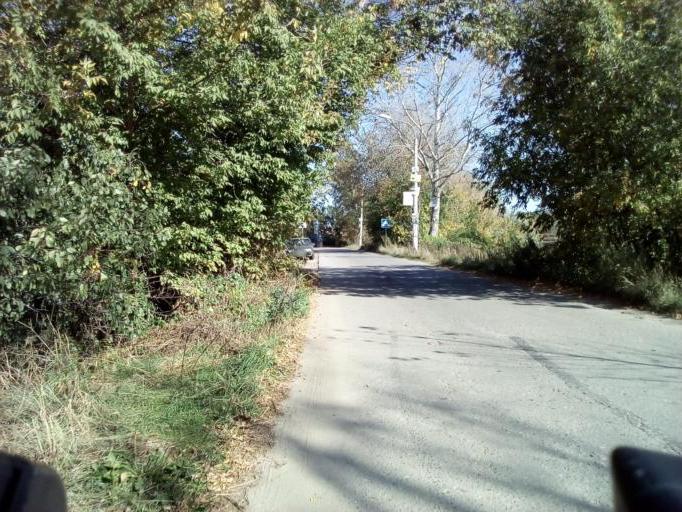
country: RU
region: Moskovskaya
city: Ramenskoye
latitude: 55.5459
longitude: 38.2894
